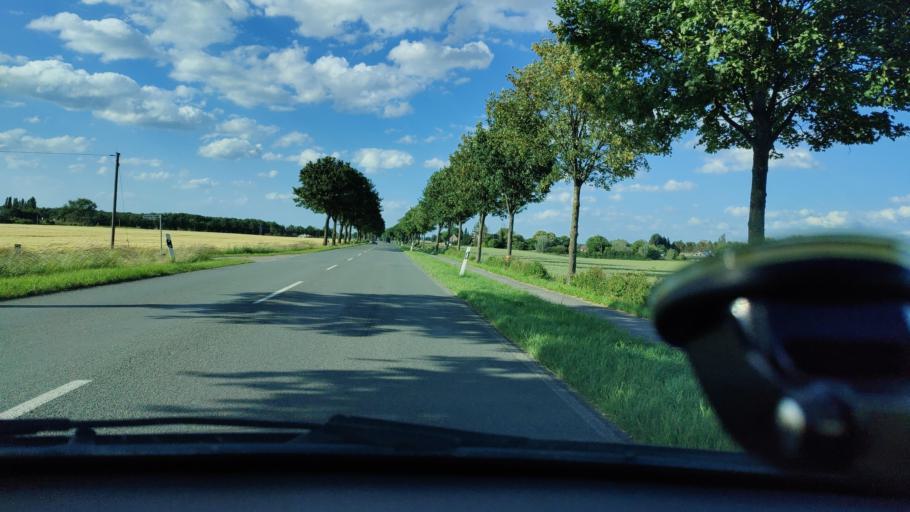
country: DE
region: North Rhine-Westphalia
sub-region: Regierungsbezirk Dusseldorf
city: Kamp-Lintfort
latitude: 51.5372
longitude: 6.5324
